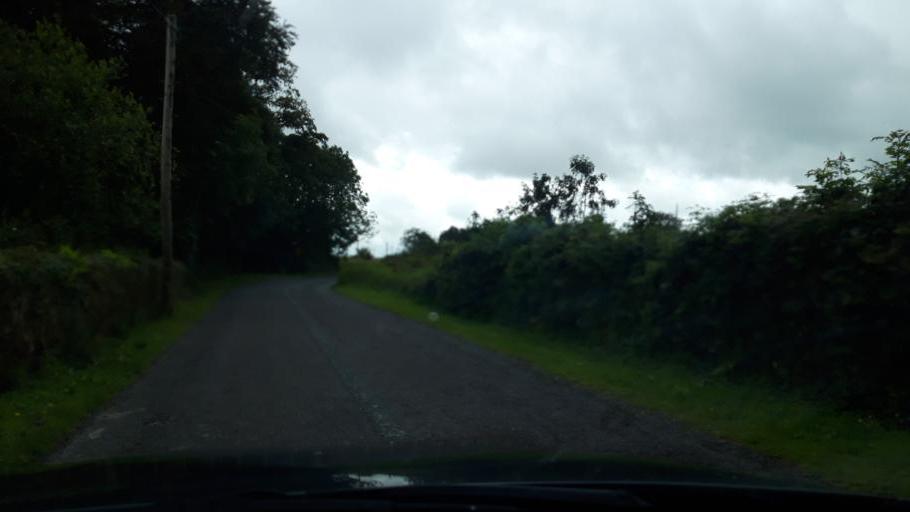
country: IE
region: Munster
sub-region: County Cork
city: Youghal
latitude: 52.1328
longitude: -7.9510
